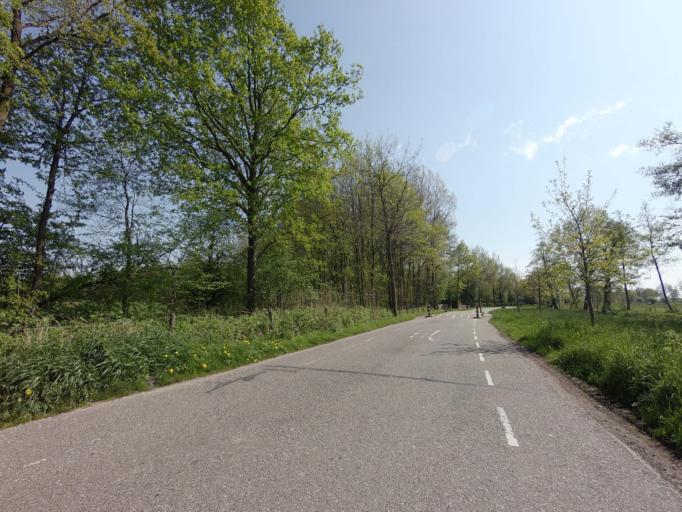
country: NL
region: Utrecht
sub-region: Gemeente Utrechtse Heuvelrug
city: Driebergen-Rijsenburg
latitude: 52.0541
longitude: 5.2454
